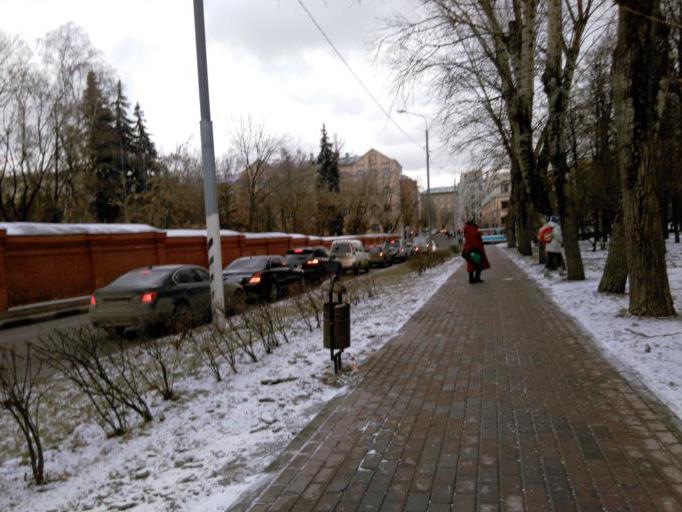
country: RU
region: Moscow
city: Novyye Cheremushki
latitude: 55.7116
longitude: 37.6008
